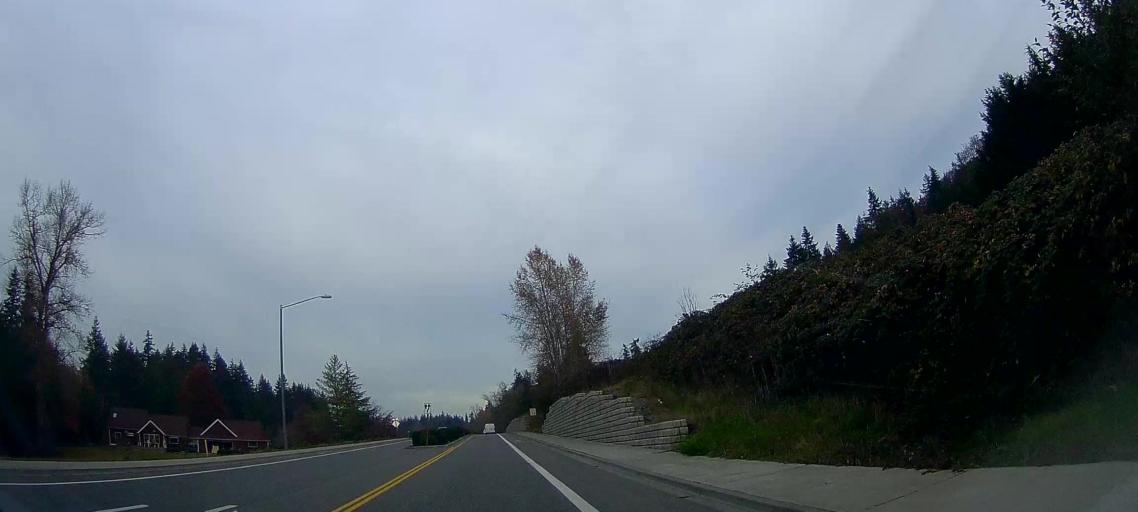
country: US
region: Washington
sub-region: Skagit County
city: Mount Vernon
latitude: 48.4006
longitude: -122.3178
